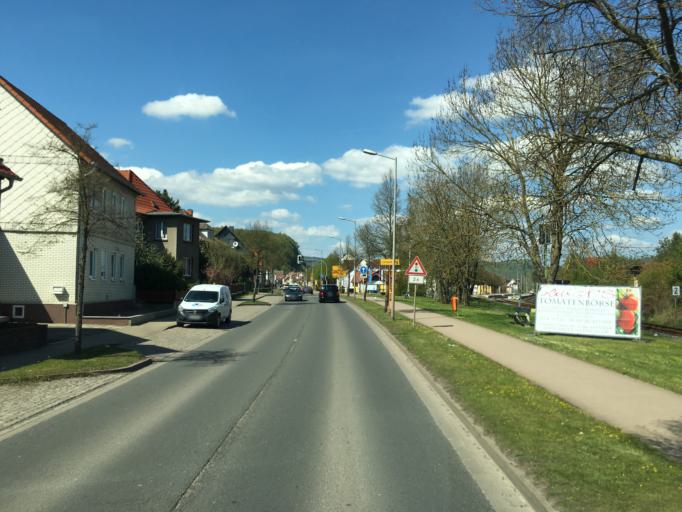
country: DE
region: Thuringia
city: Niedersachswerfen
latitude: 51.5479
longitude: 10.7686
